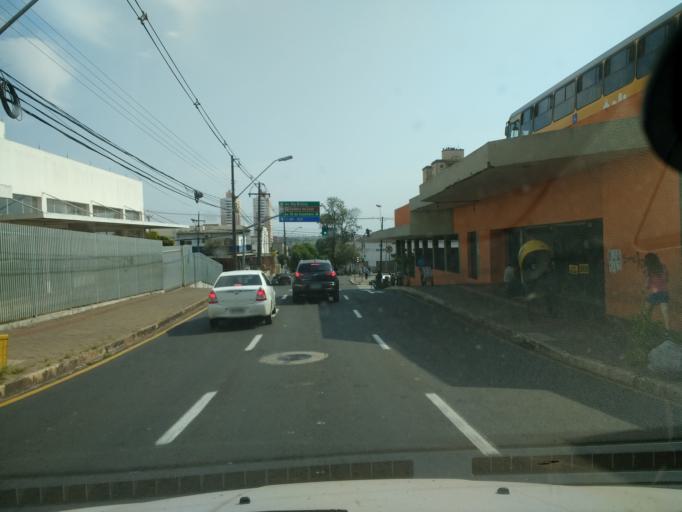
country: BR
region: Parana
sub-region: Londrina
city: Londrina
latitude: -23.3083
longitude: -51.1615
